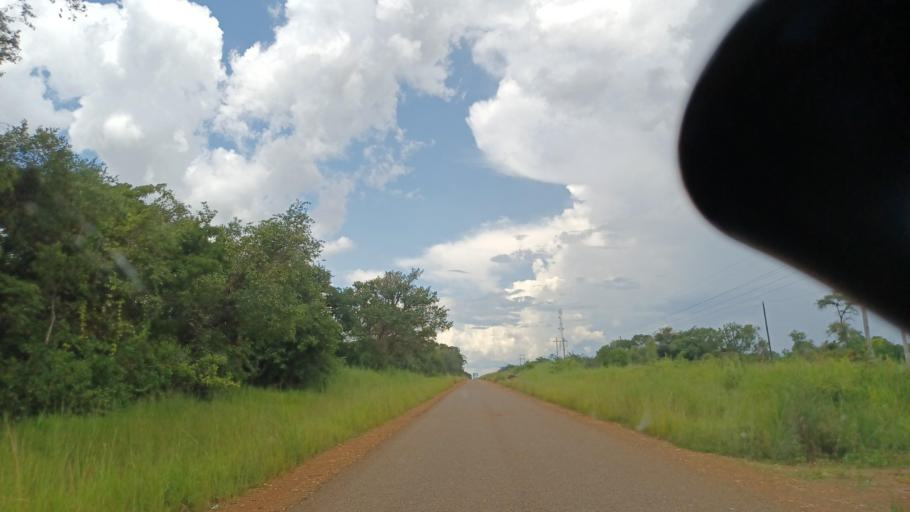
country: ZM
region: North-Western
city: Kasempa
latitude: -12.7914
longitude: 26.0142
